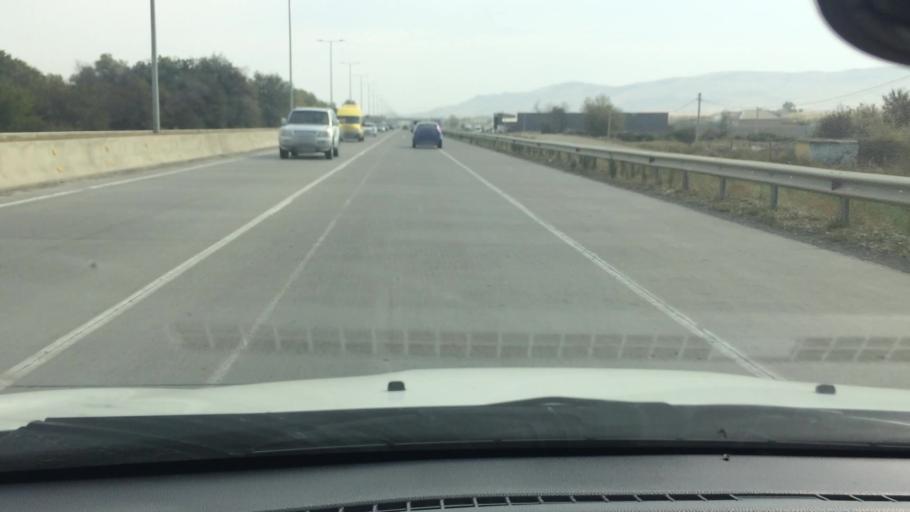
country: GE
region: Kvemo Kartli
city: Rust'avi
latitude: 41.6199
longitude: 44.9277
